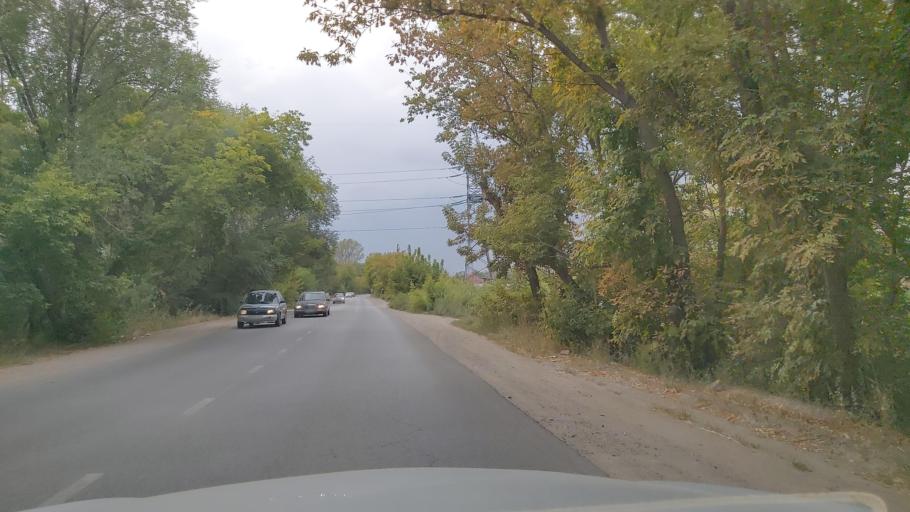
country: KZ
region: Almaty Oblysy
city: Energeticheskiy
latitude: 43.4032
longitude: 77.0309
